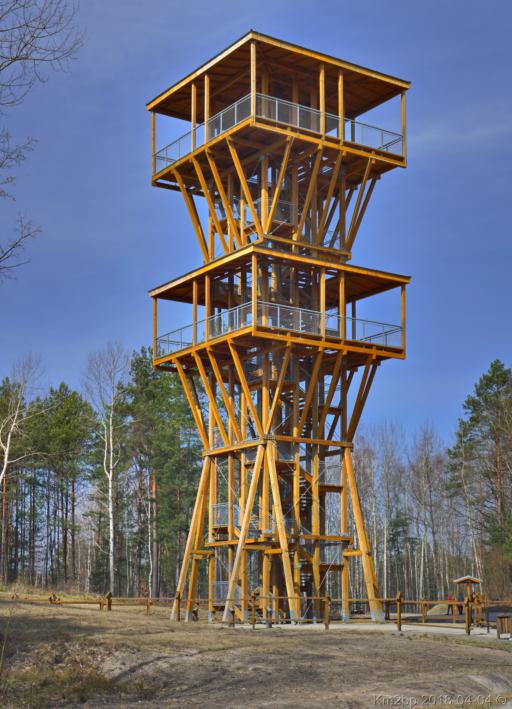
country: PL
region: Lubusz
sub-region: Powiat zarski
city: Leknica
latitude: 51.5420
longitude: 14.7750
